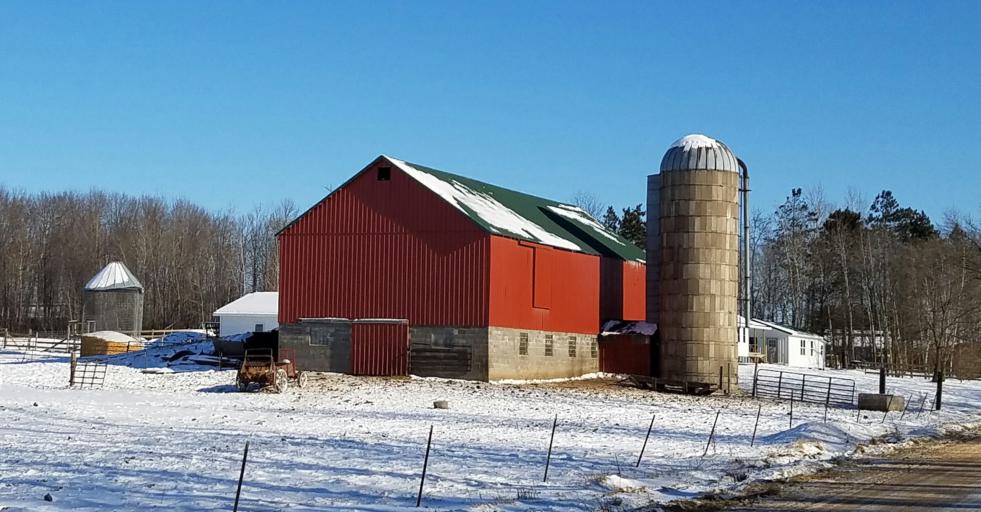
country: US
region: Wisconsin
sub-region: Clark County
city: Loyal
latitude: 44.5683
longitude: -90.3902
